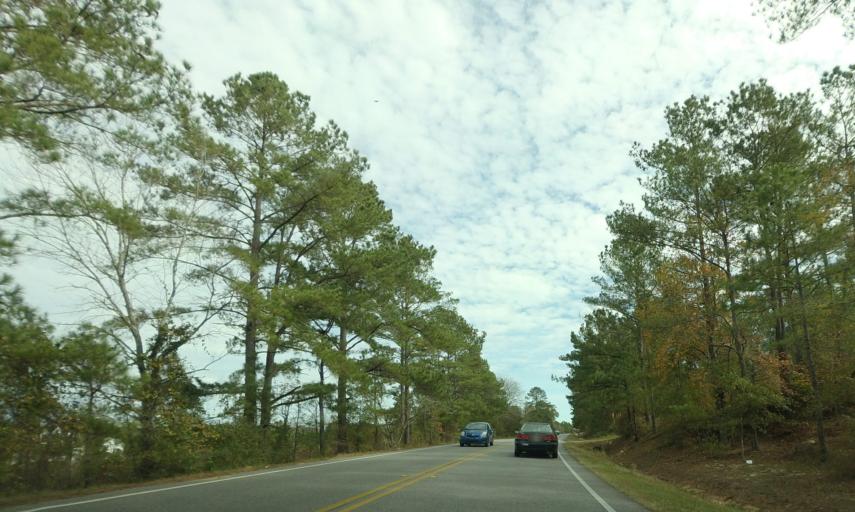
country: US
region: Georgia
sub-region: Dodge County
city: Chester
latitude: 32.4096
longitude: -83.2534
